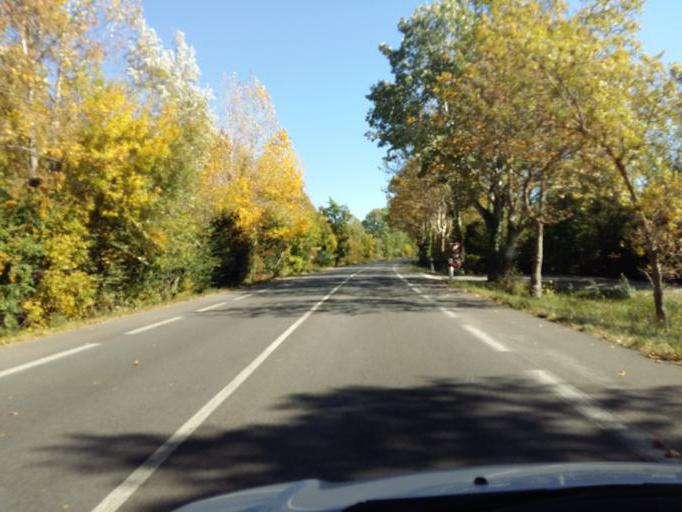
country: FR
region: Provence-Alpes-Cote d'Azur
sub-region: Departement du Vaucluse
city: Merindol
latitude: 43.7551
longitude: 5.2317
